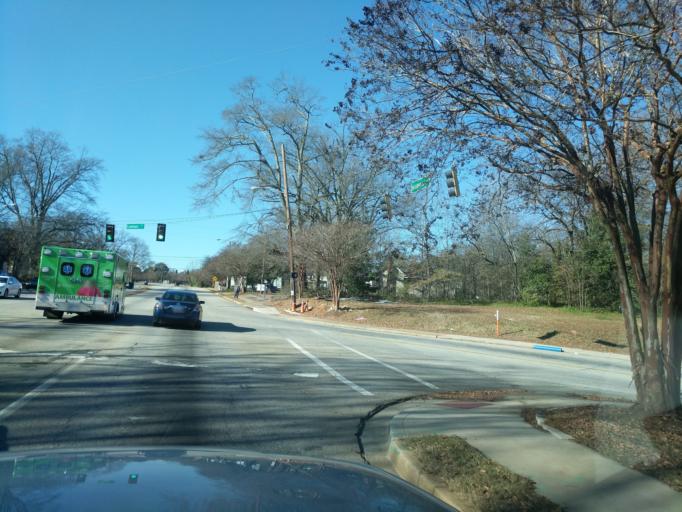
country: US
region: South Carolina
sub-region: Greenville County
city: Judson
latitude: 34.8462
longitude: -82.4140
